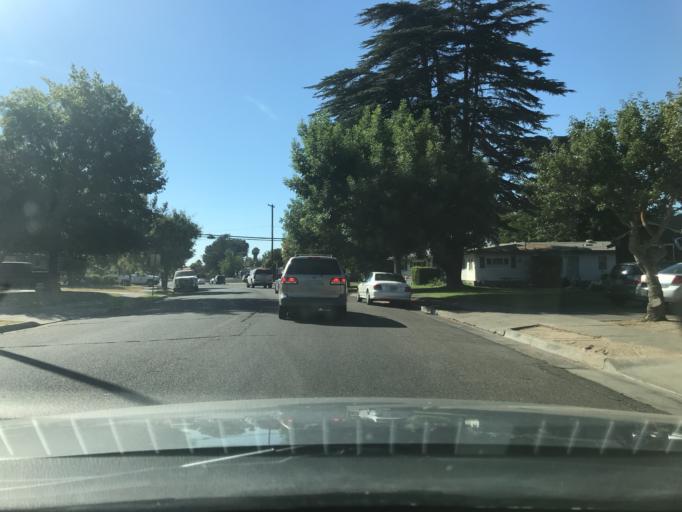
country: US
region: California
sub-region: Merced County
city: Atwater
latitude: 37.3519
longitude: -120.6020
